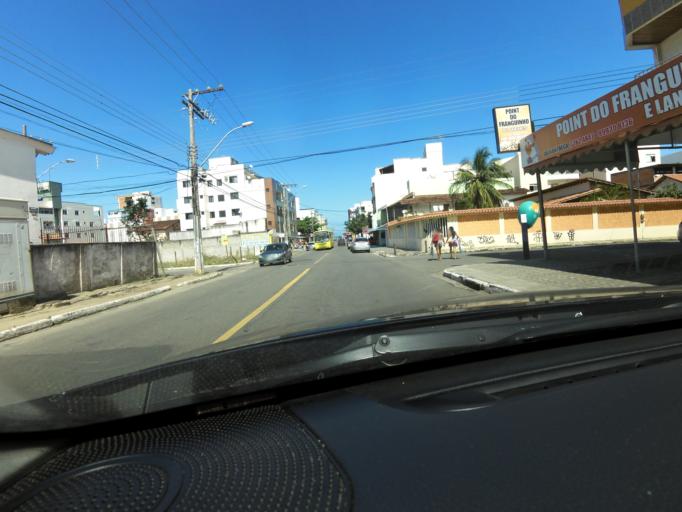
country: BR
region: Espirito Santo
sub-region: Guarapari
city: Guarapari
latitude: -20.6487
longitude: -40.4797
